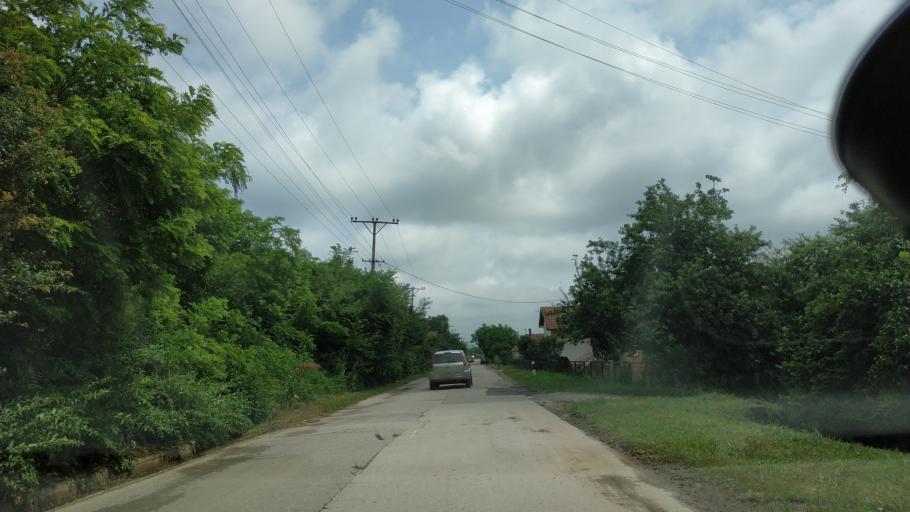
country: RS
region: Central Serbia
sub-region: Nisavski Okrug
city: Aleksinac
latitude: 43.4390
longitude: 21.7062
